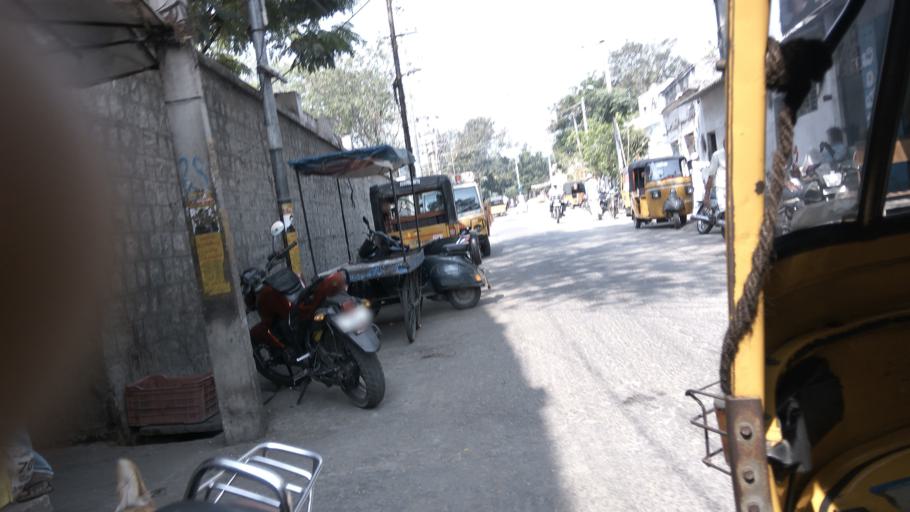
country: IN
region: Andhra Pradesh
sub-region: Chittoor
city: Tirupati
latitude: 13.6316
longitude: 79.4136
